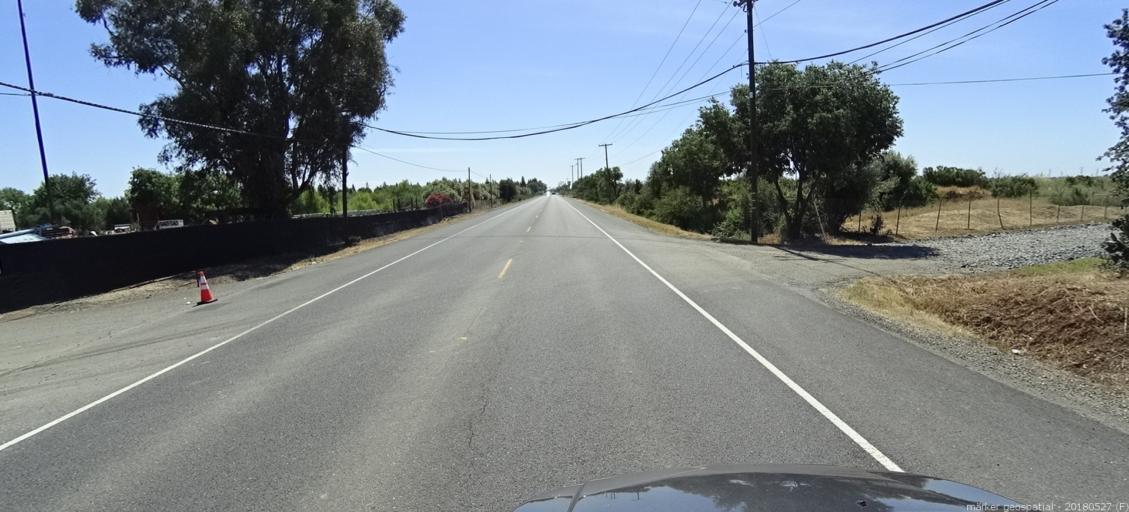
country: US
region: California
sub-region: Sacramento County
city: Rosemont
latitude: 38.5407
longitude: -121.3778
